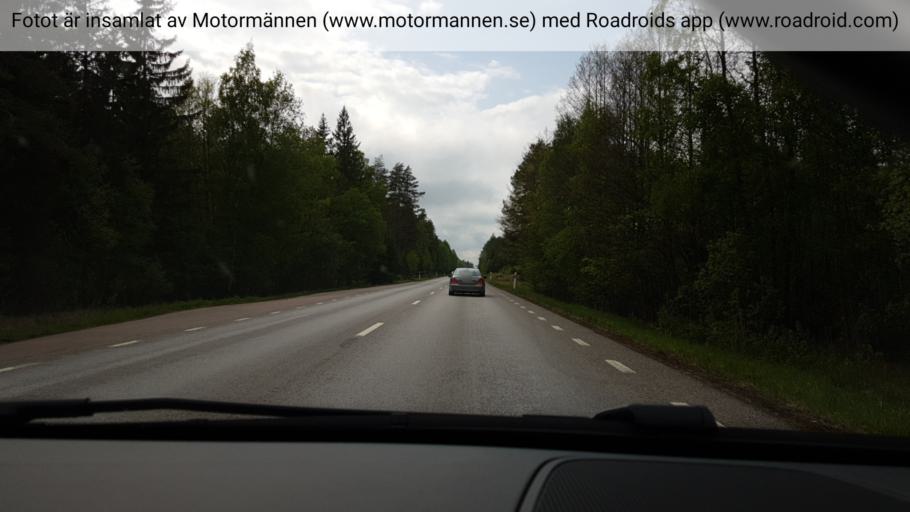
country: SE
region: Uppsala
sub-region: Osthammars Kommun
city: Osterbybruk
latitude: 60.1621
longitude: 18.0350
